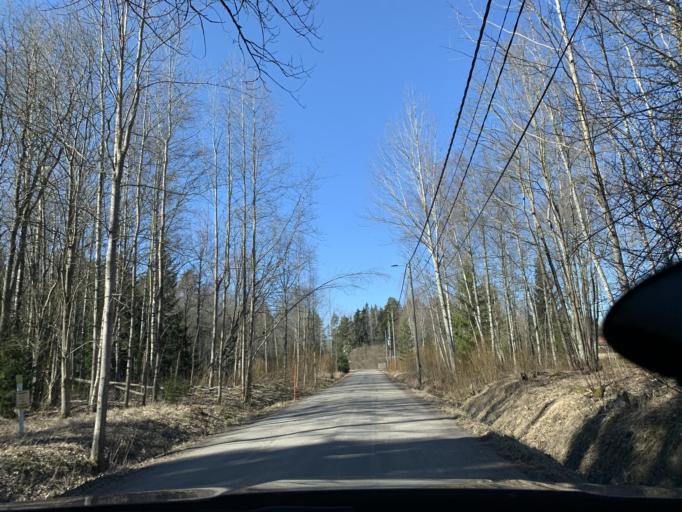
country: FI
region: Uusimaa
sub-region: Helsinki
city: Espoo
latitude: 60.1705
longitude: 24.5868
